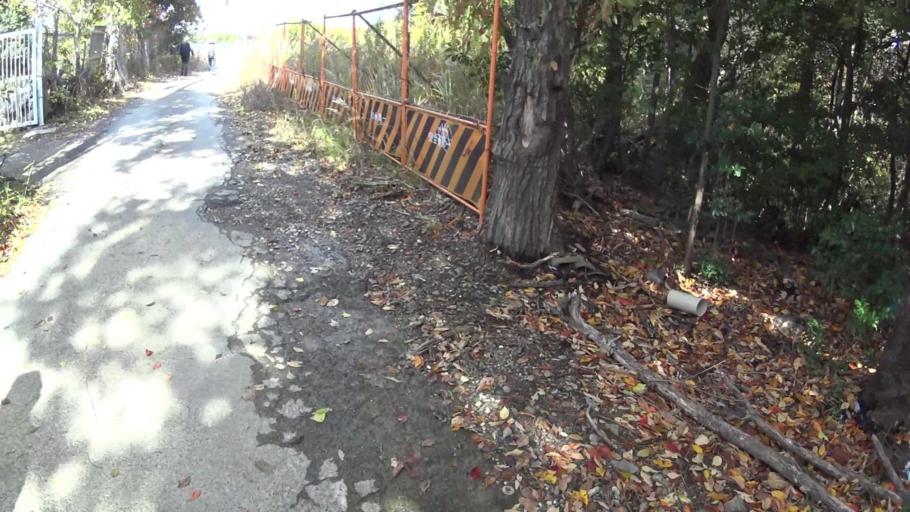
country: JP
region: Kyoto
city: Uji
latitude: 34.9473
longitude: 135.7908
